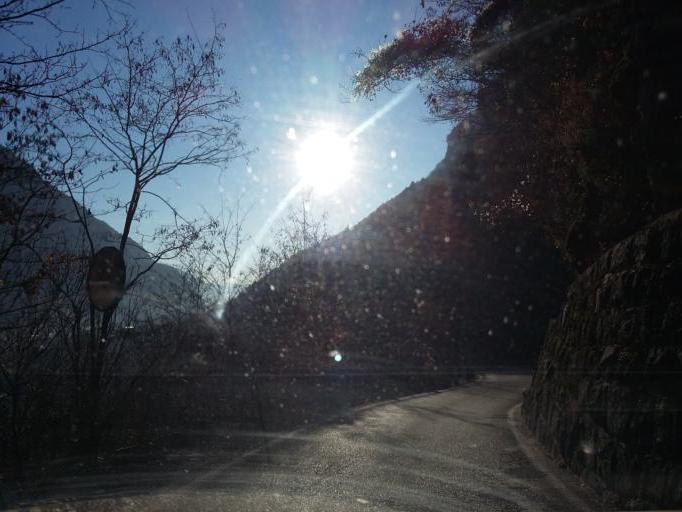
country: IT
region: Trentino-Alto Adige
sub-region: Provincia di Trento
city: Brione
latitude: 45.8933
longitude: 10.6004
